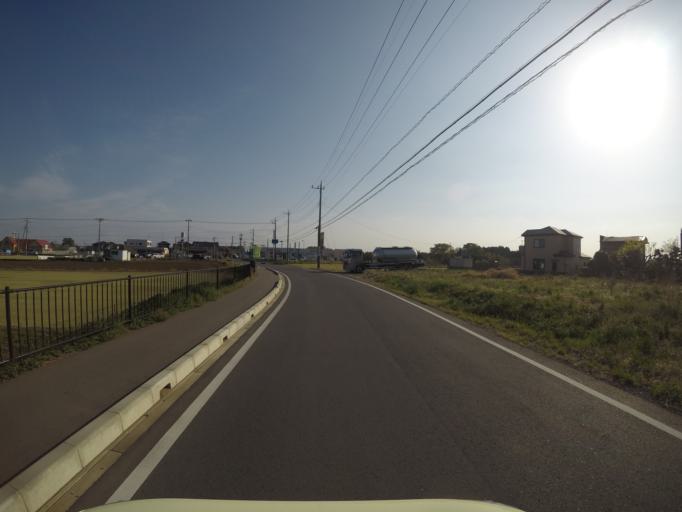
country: JP
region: Ibaraki
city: Ishige
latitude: 36.1497
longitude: 140.0153
